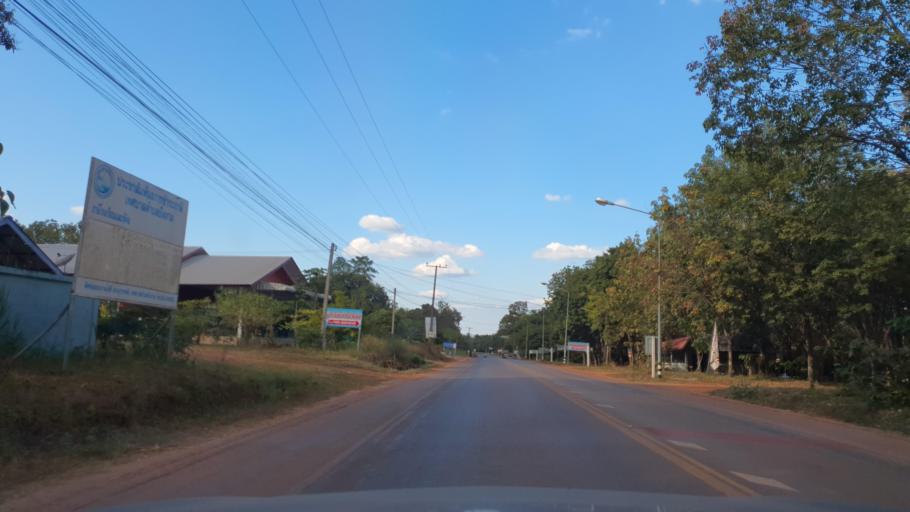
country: TH
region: Nong Khai
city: Bueng Khong Long
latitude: 17.9832
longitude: 104.0247
